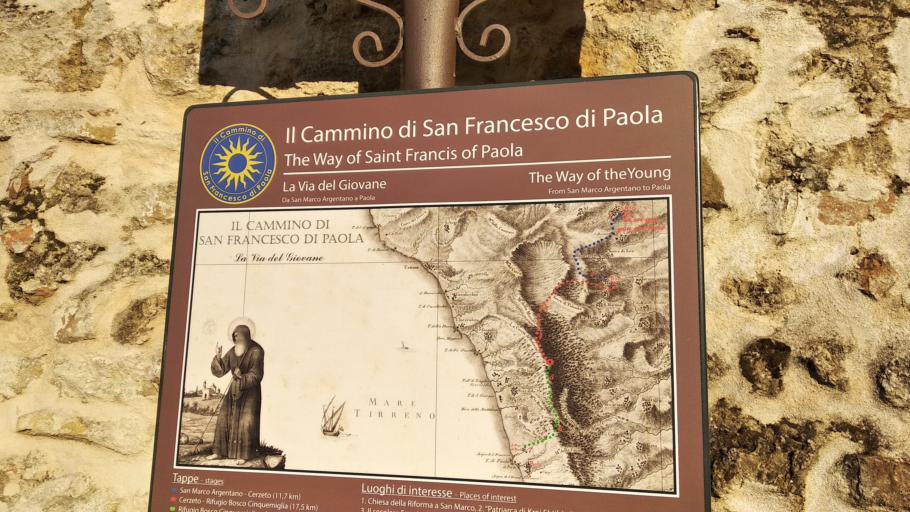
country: IT
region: Calabria
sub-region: Provincia di Cosenza
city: San Marco Argentano
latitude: 39.5565
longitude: 16.1233
